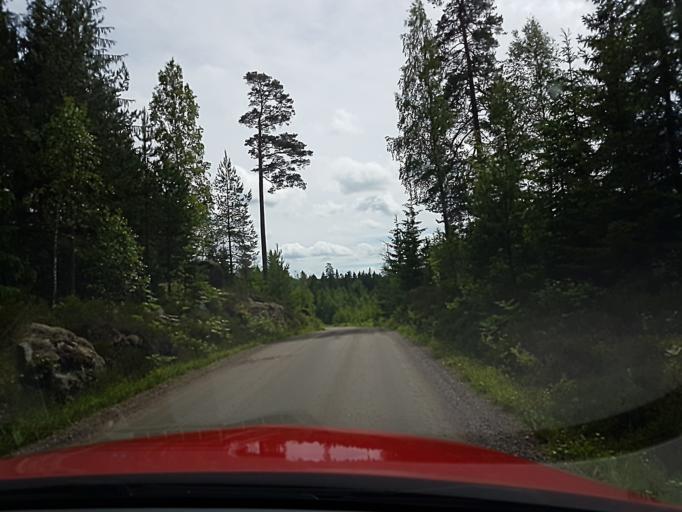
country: SE
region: Vaestra Goetaland
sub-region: Karlsborgs Kommun
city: Karlsborg
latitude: 58.7418
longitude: 14.5844
